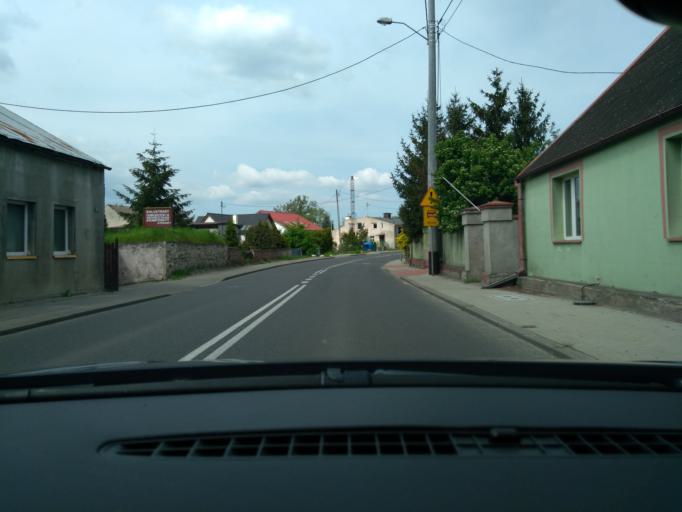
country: PL
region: West Pomeranian Voivodeship
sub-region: Powiat gryfinski
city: Gryfino
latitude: 53.3206
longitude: 14.5377
